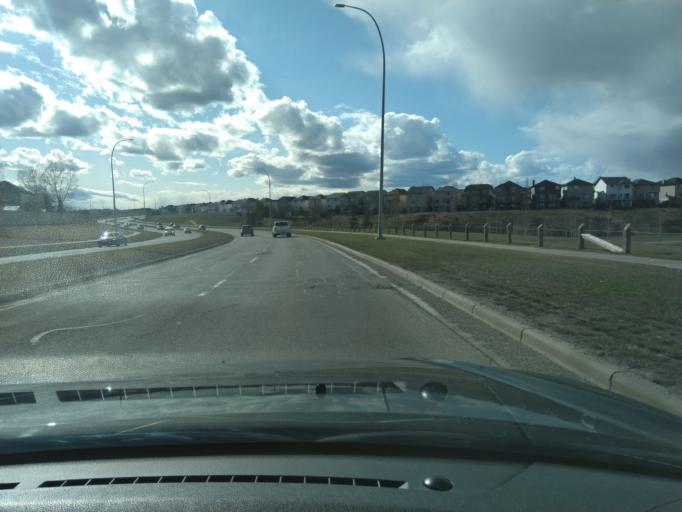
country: CA
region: Alberta
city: Calgary
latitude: 51.1434
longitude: -114.1875
